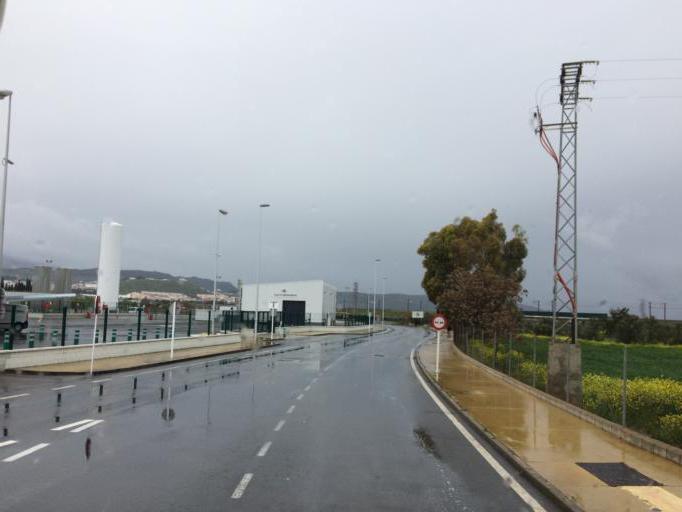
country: ES
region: Andalusia
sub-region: Provincia de Malaga
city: Antequera
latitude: 37.0384
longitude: -4.5305
